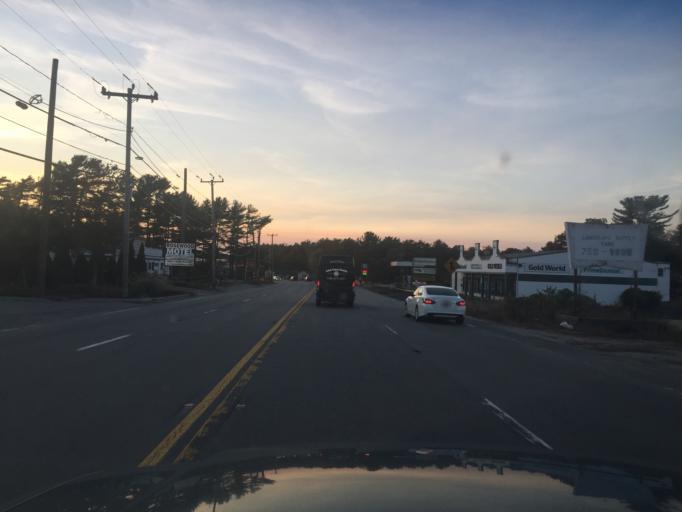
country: US
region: Massachusetts
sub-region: Plymouth County
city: Onset
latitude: 41.7551
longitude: -70.6402
